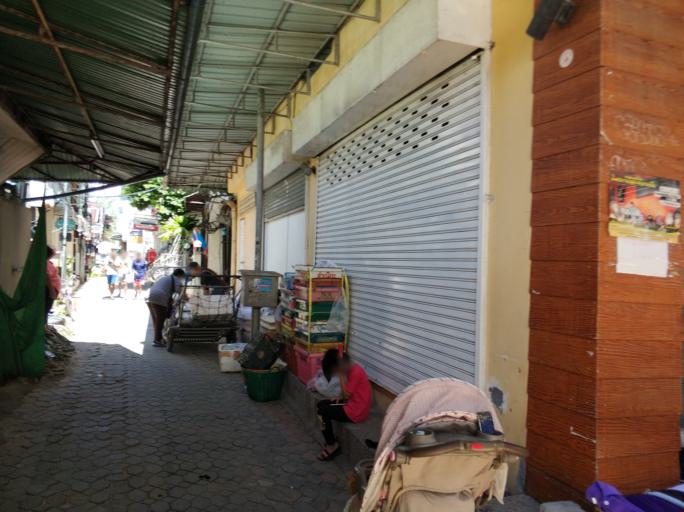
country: TH
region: Phangnga
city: Ban Phru Nai
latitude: 7.7393
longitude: 98.7718
